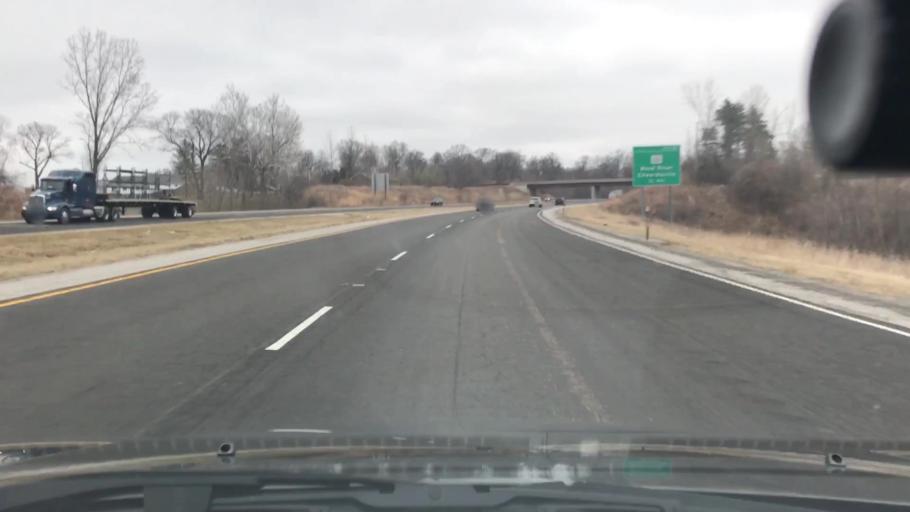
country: US
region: Illinois
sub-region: Madison County
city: Roxana
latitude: 38.8658
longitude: -90.0549
